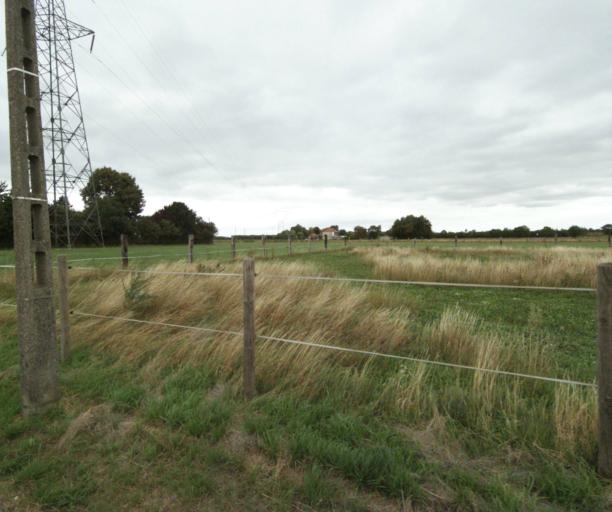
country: FR
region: Nord-Pas-de-Calais
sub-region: Departement du Nord
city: Fretin
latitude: 50.5609
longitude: 3.1558
